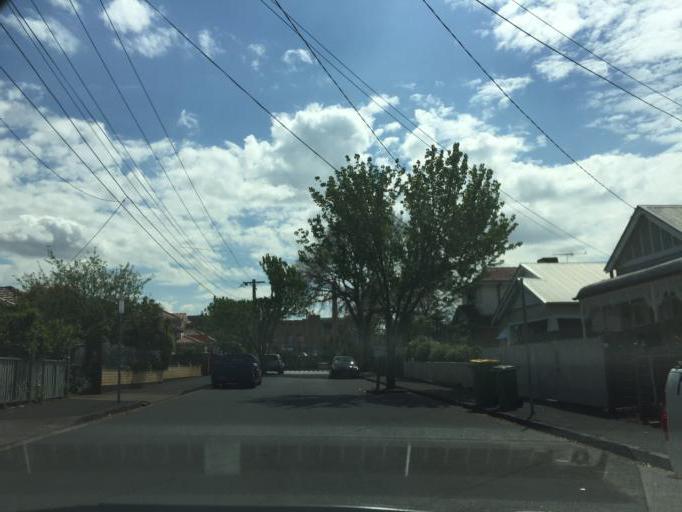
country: AU
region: Victoria
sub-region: Maribyrnong
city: West Footscray
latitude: -37.7950
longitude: 144.8863
